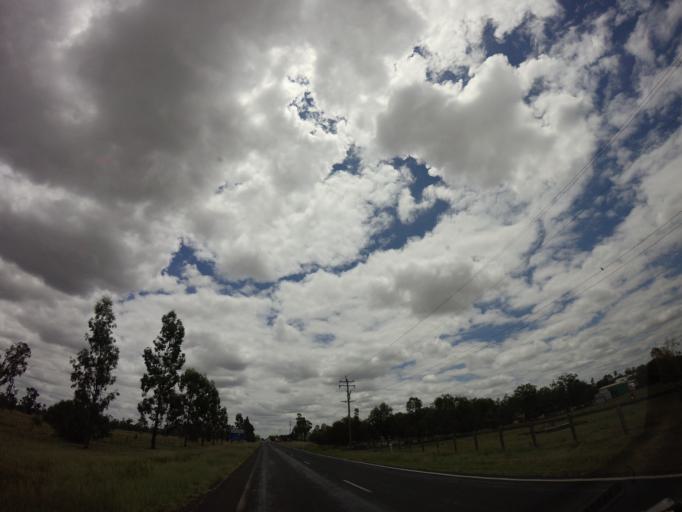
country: AU
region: Queensland
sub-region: Goondiwindi
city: Goondiwindi
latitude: -28.5152
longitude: 150.2889
